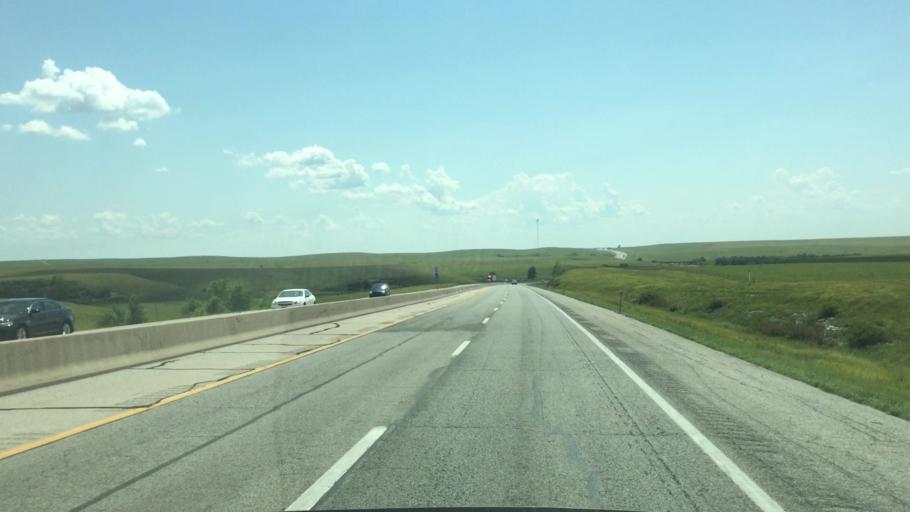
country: US
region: Kansas
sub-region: Chase County
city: Cottonwood Falls
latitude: 38.1822
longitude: -96.4607
